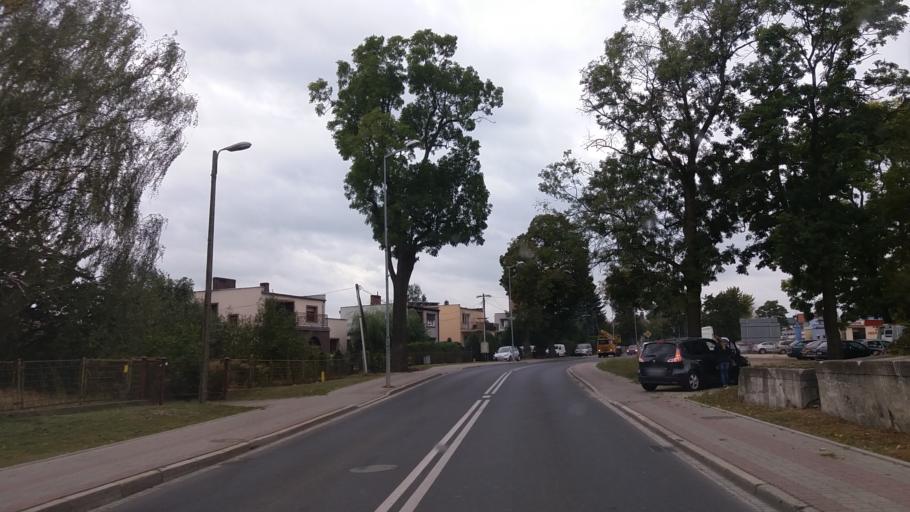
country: PL
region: Lubusz
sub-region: Powiat strzelecko-drezdenecki
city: Strzelce Krajenskie
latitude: 52.8751
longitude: 15.5267
